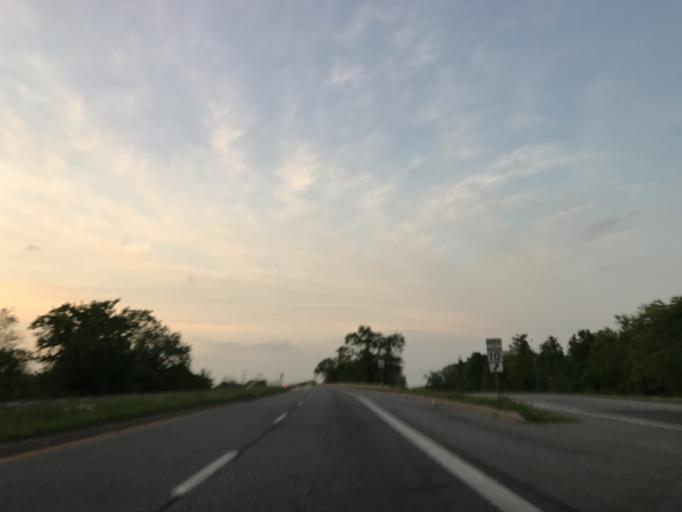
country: US
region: Maryland
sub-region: Anne Arundel County
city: Glen Burnie
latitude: 39.1752
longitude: -76.6057
